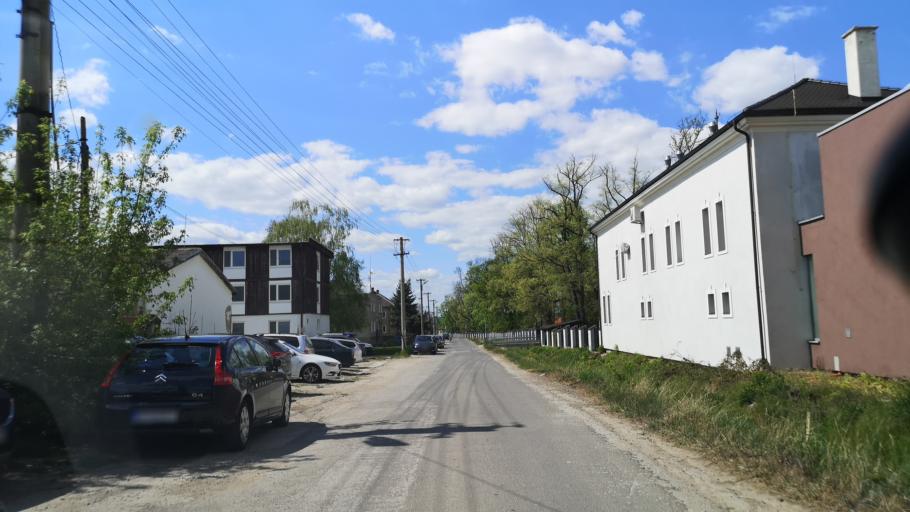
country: SK
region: Nitriansky
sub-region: Okres Nitra
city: Nitra
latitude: 48.4634
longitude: 18.1486
